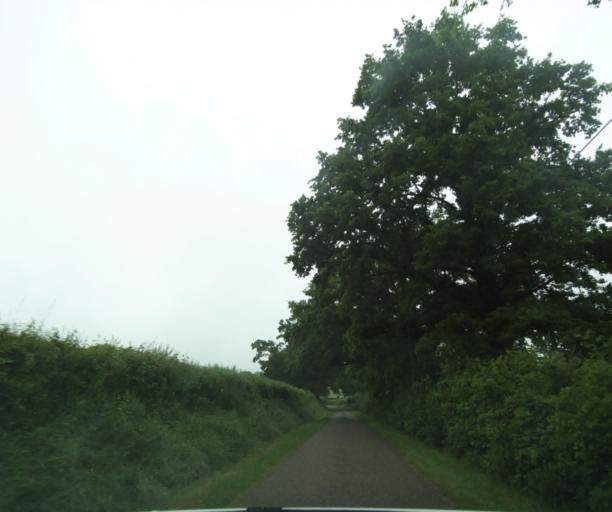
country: FR
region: Bourgogne
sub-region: Departement de Saone-et-Loire
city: Paray-le-Monial
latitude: 46.4037
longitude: 4.1879
